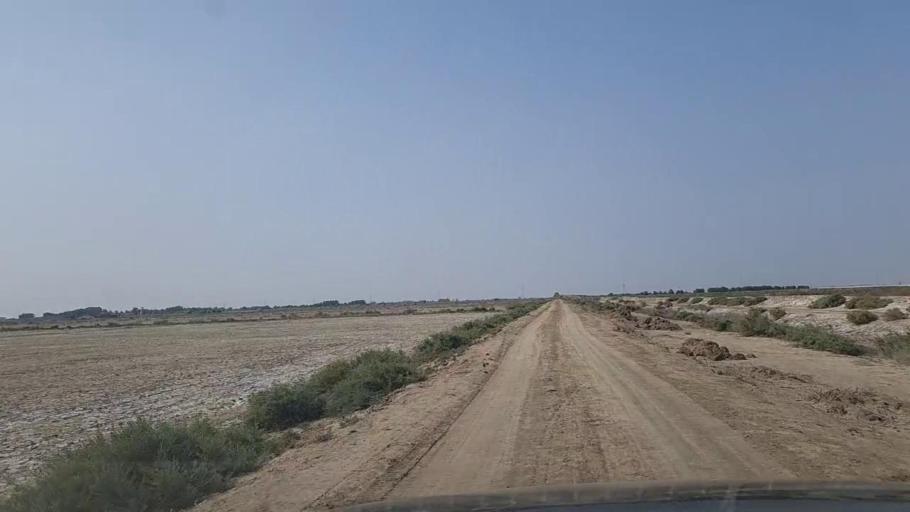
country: PK
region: Sindh
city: Gharo
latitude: 24.7046
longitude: 67.5649
